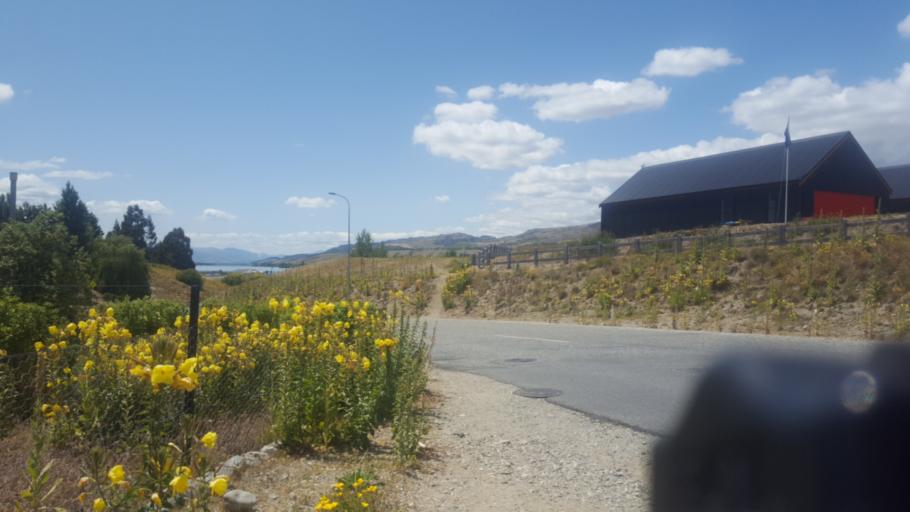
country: NZ
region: Otago
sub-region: Queenstown-Lakes District
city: Wanaka
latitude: -45.0297
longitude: 169.2058
